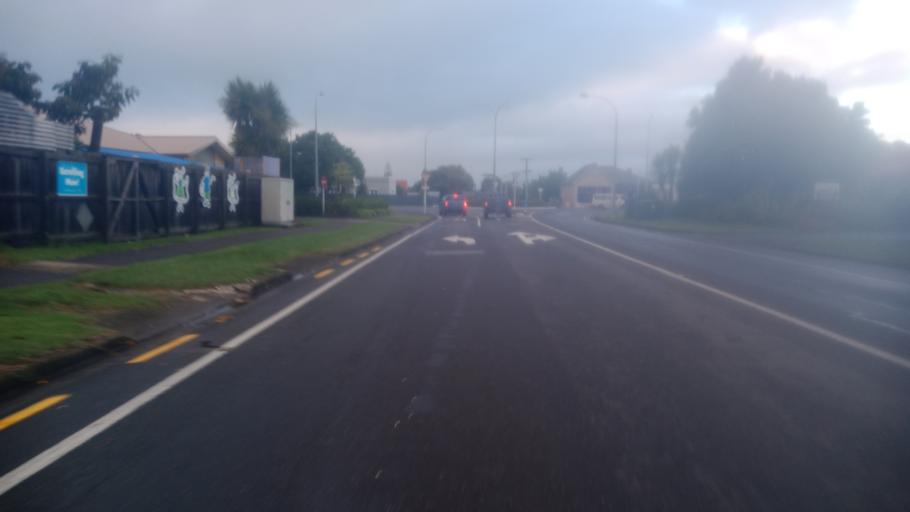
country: NZ
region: Gisborne
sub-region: Gisborne District
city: Gisborne
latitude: -38.6510
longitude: 177.9984
